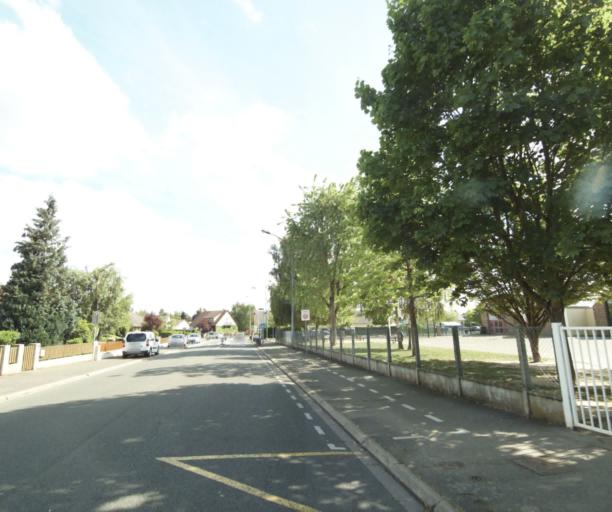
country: FR
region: Centre
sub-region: Departement d'Eure-et-Loir
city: Luce
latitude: 48.4337
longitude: 1.4499
